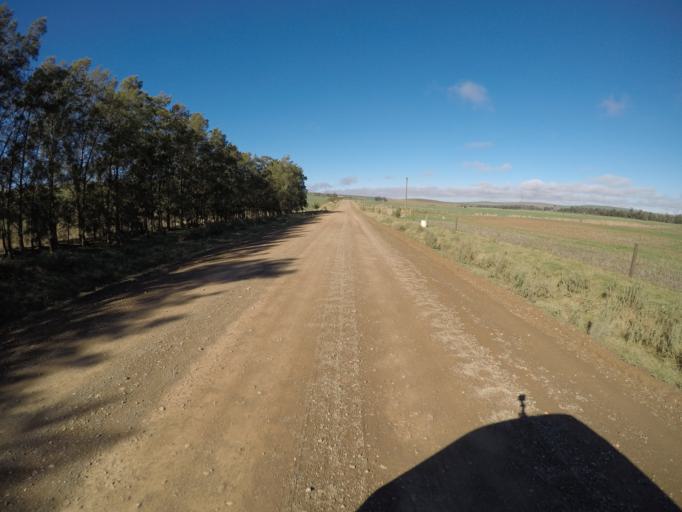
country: ZA
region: Western Cape
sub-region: Overberg District Municipality
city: Caledon
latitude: -34.1006
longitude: 19.7001
